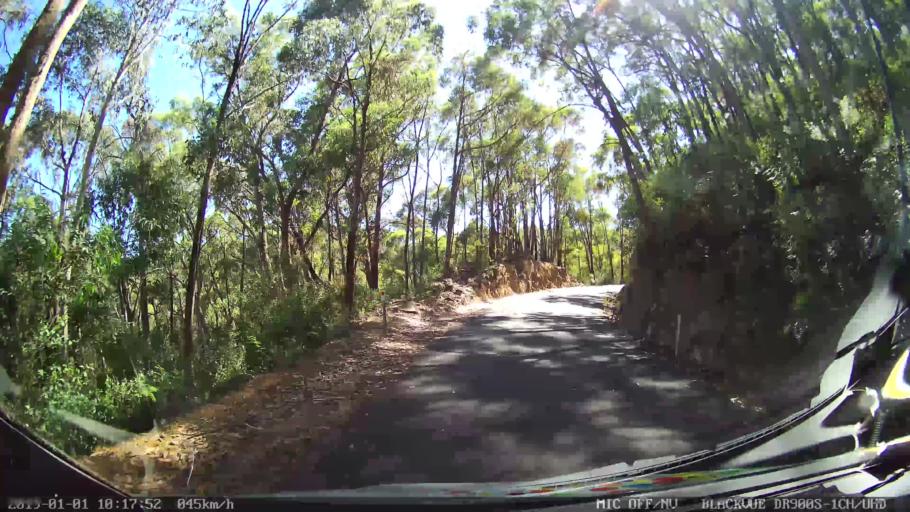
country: AU
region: New South Wales
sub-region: Snowy River
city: Jindabyne
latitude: -36.0895
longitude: 148.1786
